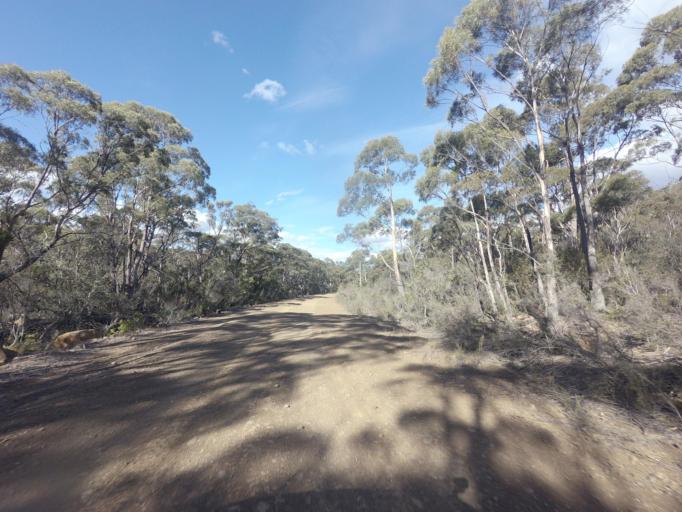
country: AU
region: Tasmania
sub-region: Break O'Day
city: St Helens
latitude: -41.8561
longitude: 148.0264
